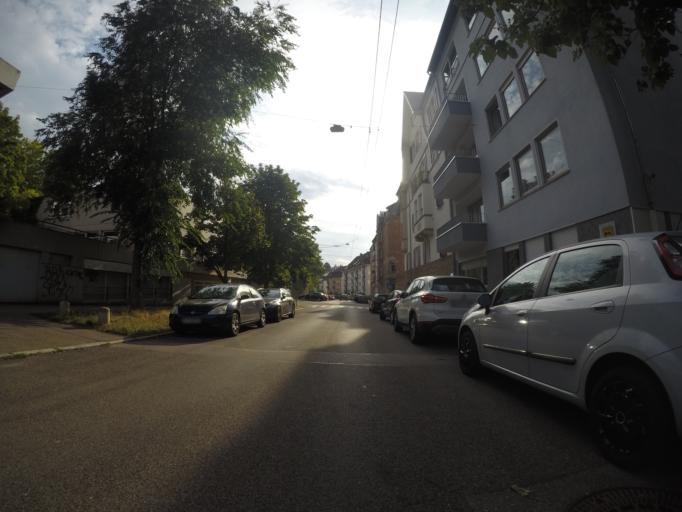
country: DE
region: Baden-Wuerttemberg
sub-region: Regierungsbezirk Stuttgart
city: Stuttgart
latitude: 48.7620
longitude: 9.1761
